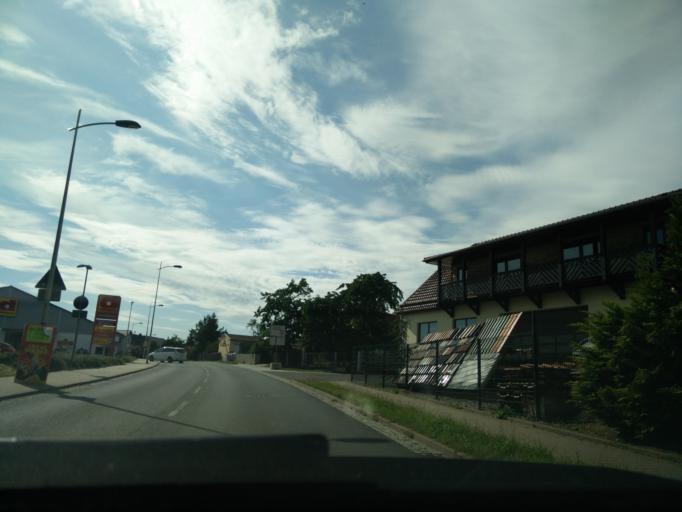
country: DE
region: Saxony
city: Bad Lausick
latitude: 51.1431
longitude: 12.6389
